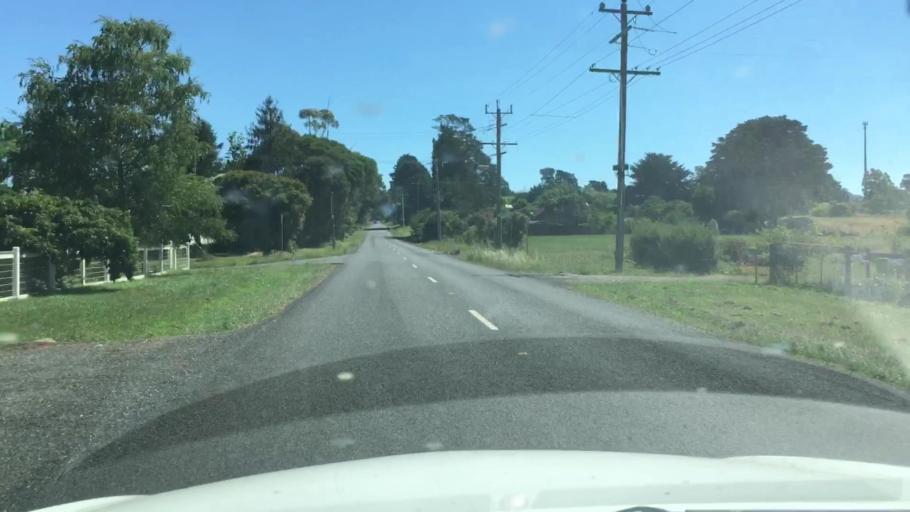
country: AU
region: Victoria
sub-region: Yarra Ranges
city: Mount Evelyn
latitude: -37.8093
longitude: 145.4304
